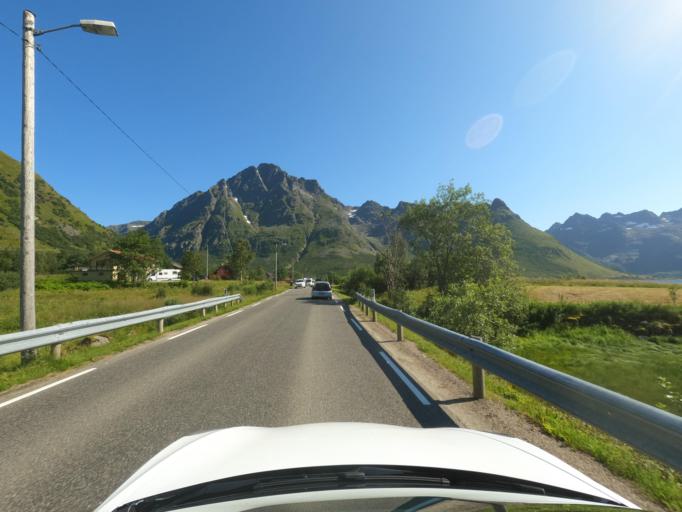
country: NO
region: Nordland
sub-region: Hadsel
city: Melbu
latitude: 68.3577
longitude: 14.7191
